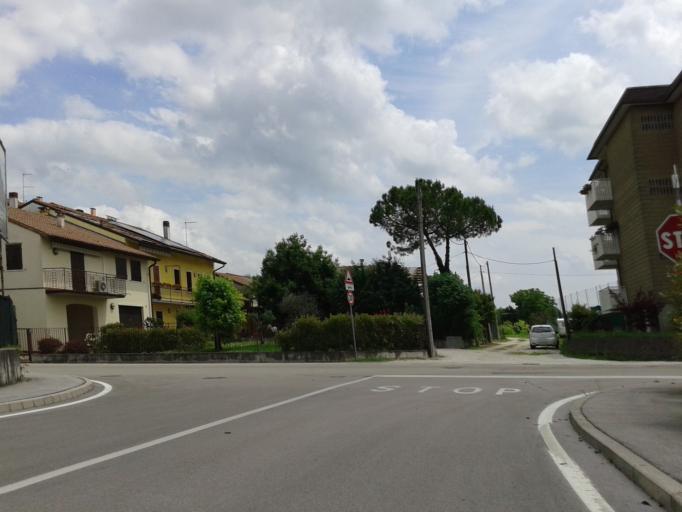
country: IT
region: Veneto
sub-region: Provincia di Vicenza
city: Monticello Conte Otto
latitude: 45.5923
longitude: 11.5514
